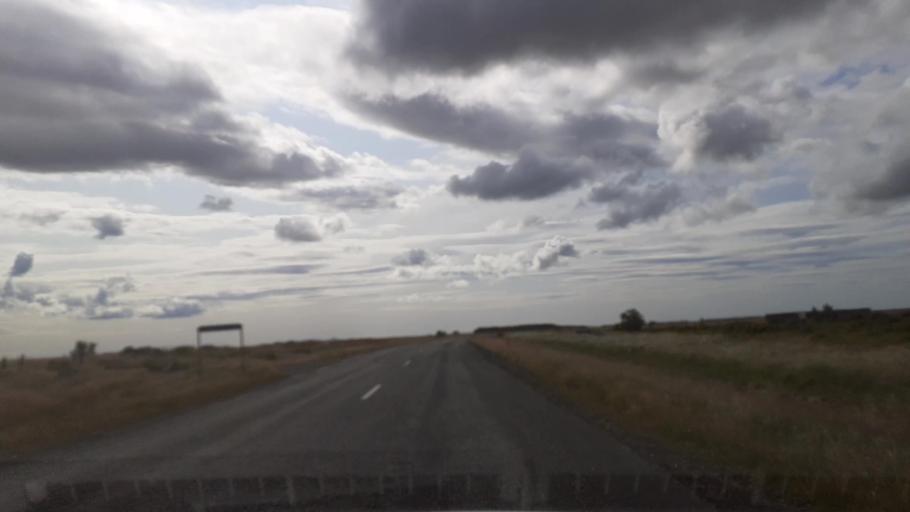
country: IS
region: South
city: Vestmannaeyjar
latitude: 63.8198
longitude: -20.4274
